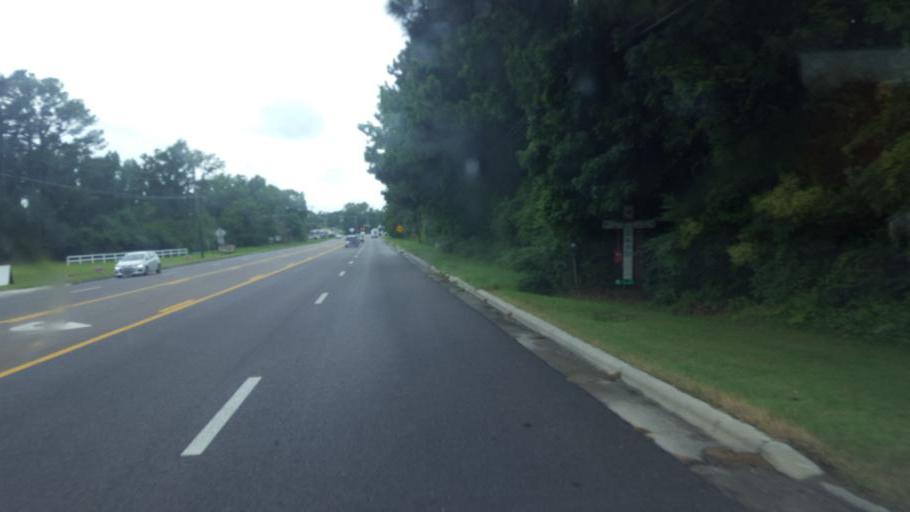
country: US
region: North Carolina
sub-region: Dare County
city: Southern Shores
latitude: 36.2448
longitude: -75.8841
